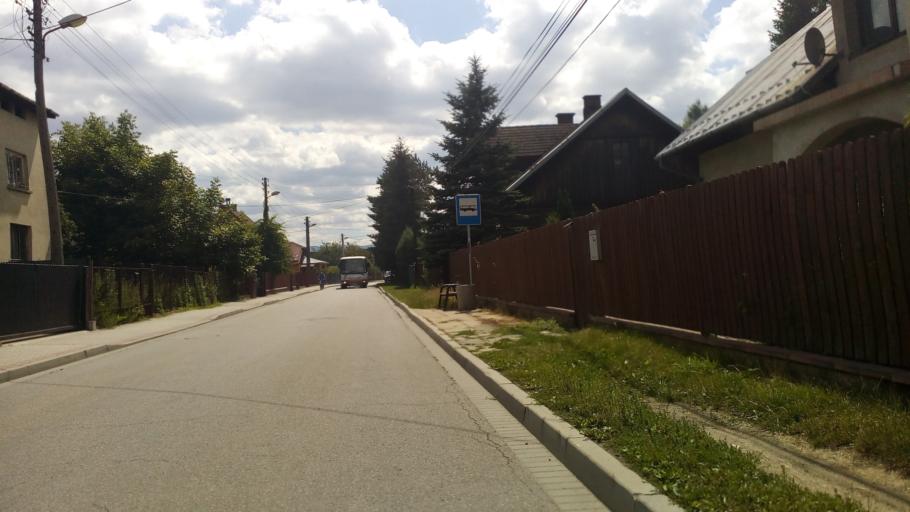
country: PL
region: Lesser Poland Voivodeship
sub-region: Powiat nowosadecki
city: Nowy Sacz
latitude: 49.6130
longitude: 20.6839
